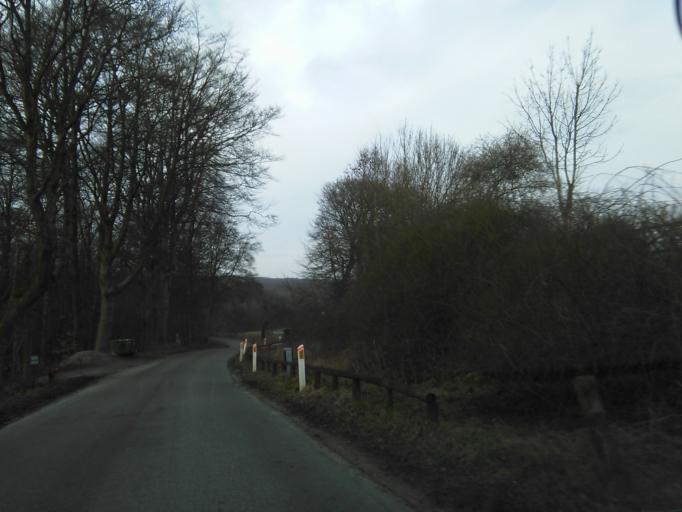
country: DK
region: Central Jutland
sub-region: Arhus Kommune
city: Beder
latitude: 56.0794
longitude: 10.2341
